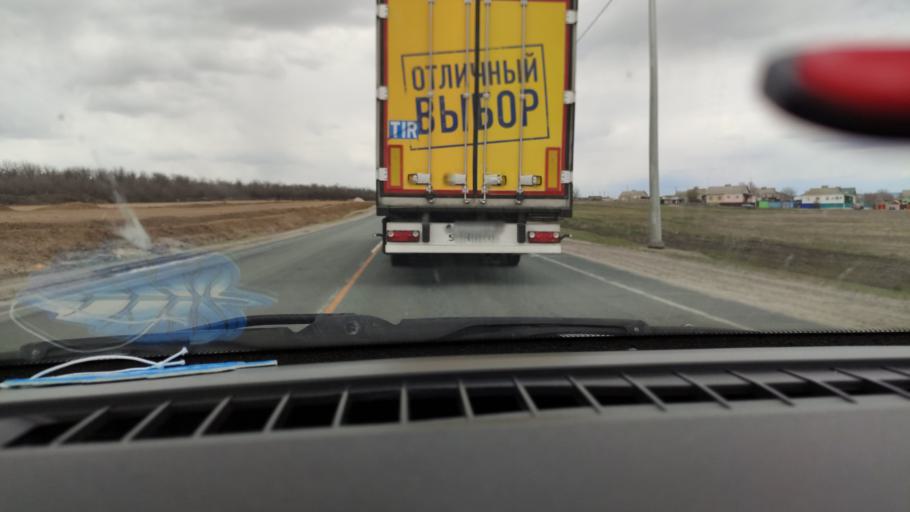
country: RU
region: Saratov
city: Sennoy
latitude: 52.1586
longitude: 47.0645
